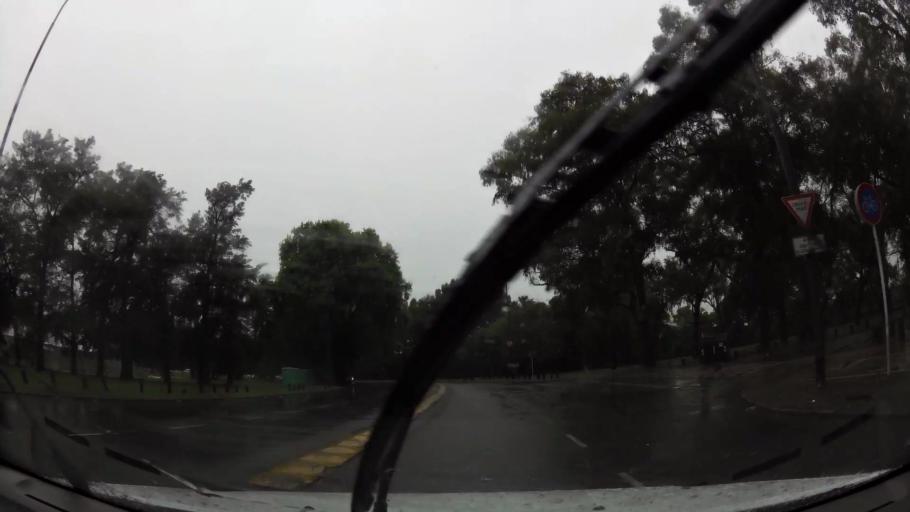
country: AR
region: Buenos Aires F.D.
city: Colegiales
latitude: -34.5638
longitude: -58.4228
